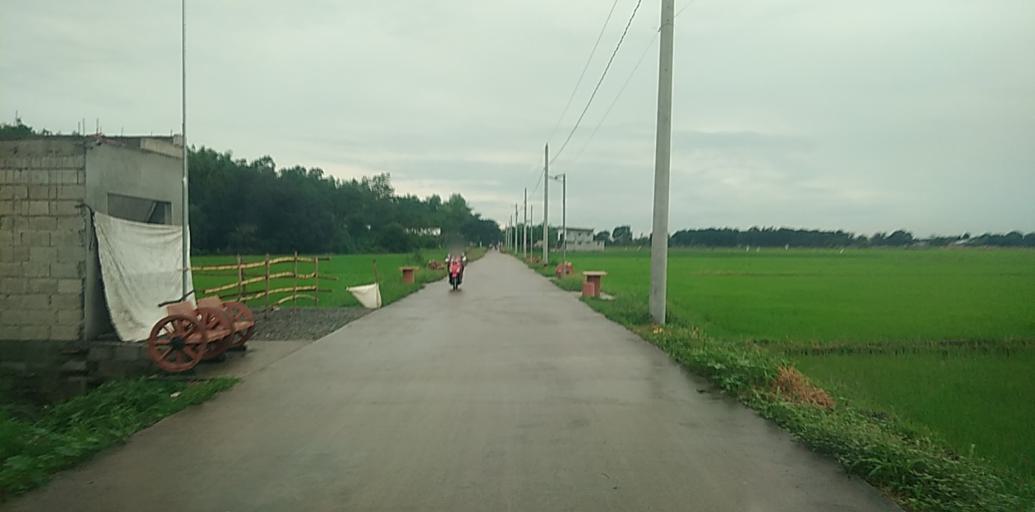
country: PH
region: Central Luzon
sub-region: Province of Pampanga
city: Arayat
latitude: 15.1615
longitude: 120.7412
